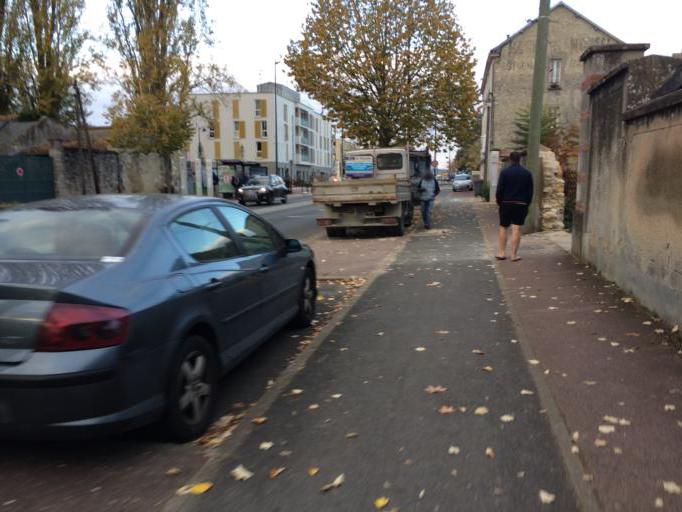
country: FR
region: Ile-de-France
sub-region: Departement de l'Essonne
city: Morigny-Champigny
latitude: 48.4487
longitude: 2.1712
